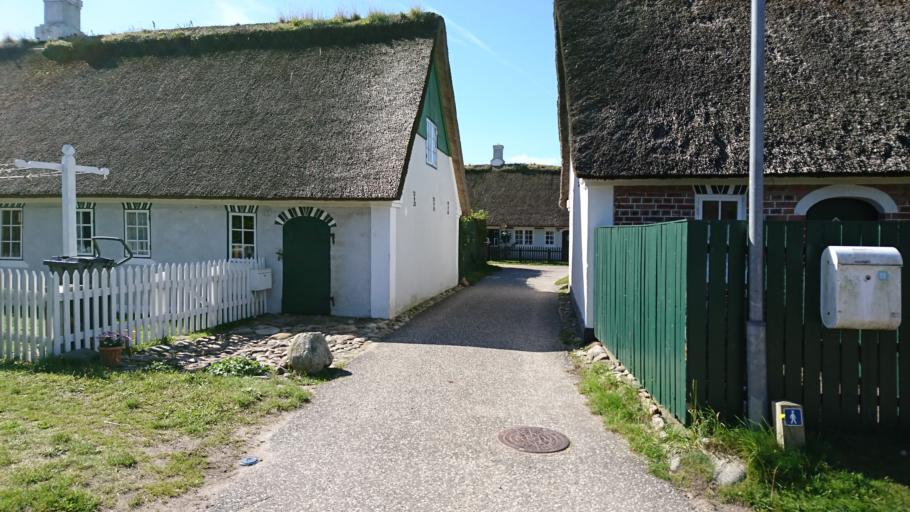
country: DK
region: South Denmark
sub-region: Esbjerg Kommune
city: Esbjerg
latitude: 55.3495
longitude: 8.4741
